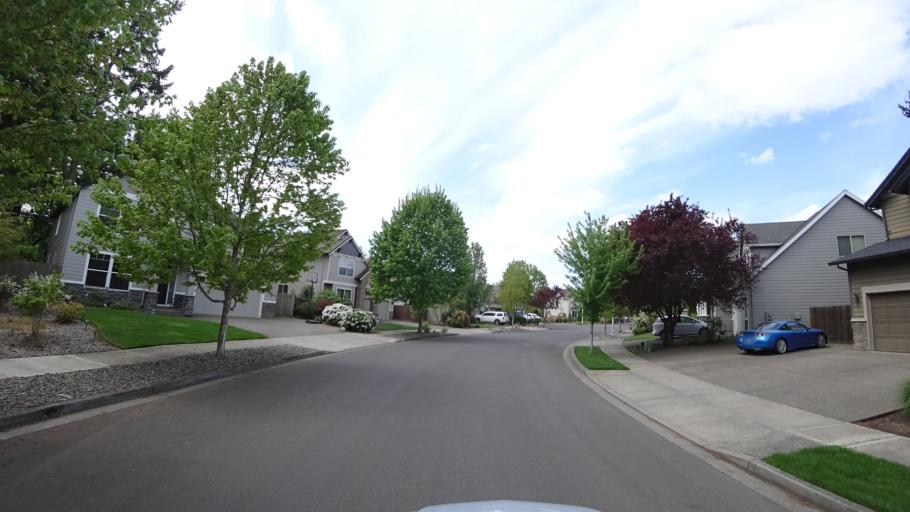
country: US
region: Oregon
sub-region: Washington County
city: Hillsboro
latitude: 45.5371
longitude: -122.9926
